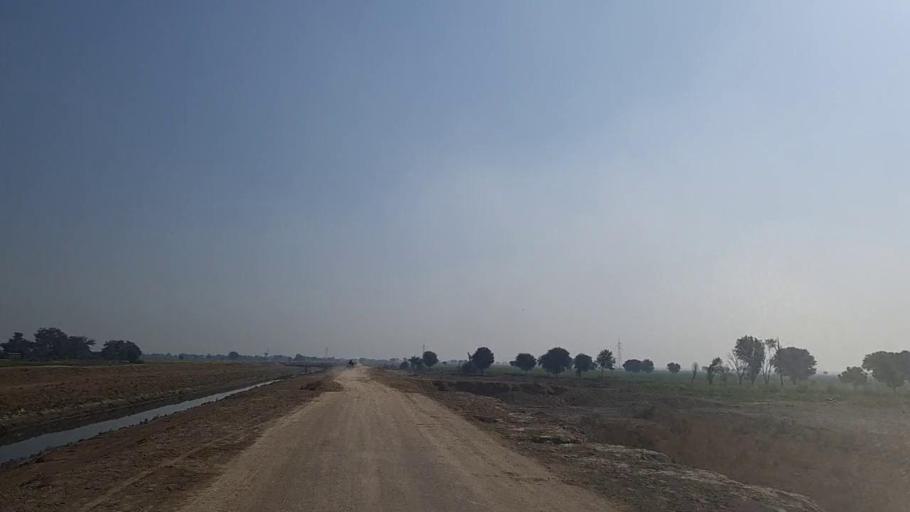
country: PK
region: Sindh
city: Shahpur Chakar
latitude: 26.1789
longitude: 68.5697
